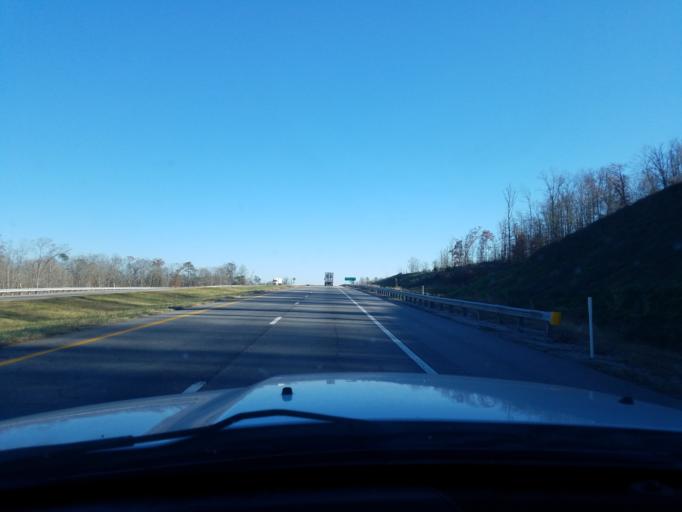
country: US
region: West Virginia
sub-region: Putnam County
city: Buffalo
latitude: 38.5542
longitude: -81.9969
